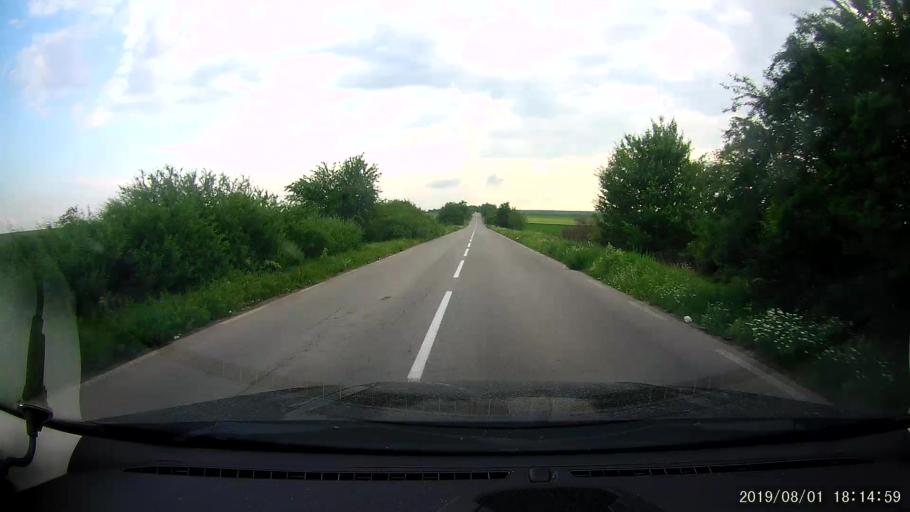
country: BG
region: Silistra
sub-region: Obshtina Dulovo
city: Dulovo
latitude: 43.7607
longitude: 27.1145
